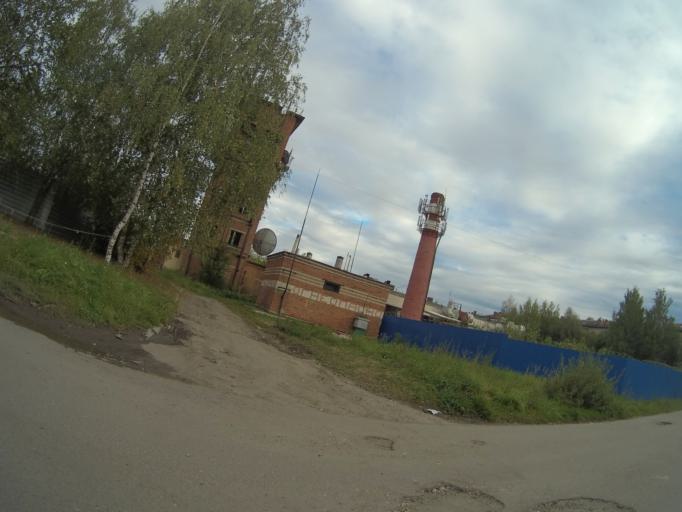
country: RU
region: Vladimir
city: Vladimir
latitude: 56.1074
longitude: 40.2846
